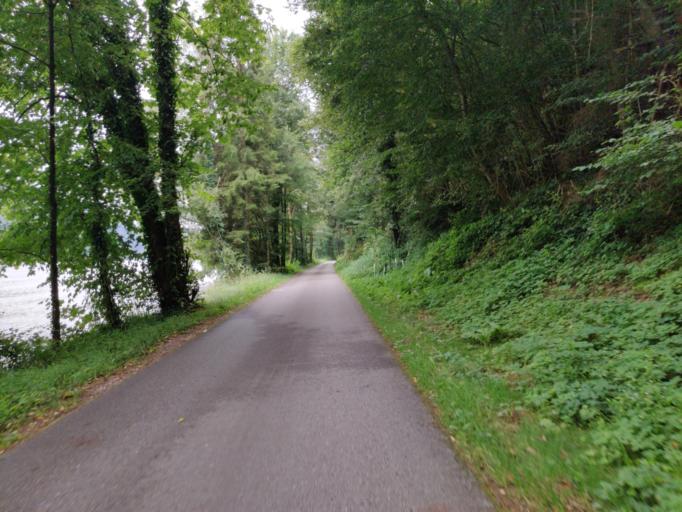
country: AT
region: Lower Austria
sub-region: Politischer Bezirk Melk
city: Nochling
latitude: 48.2176
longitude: 14.9494
